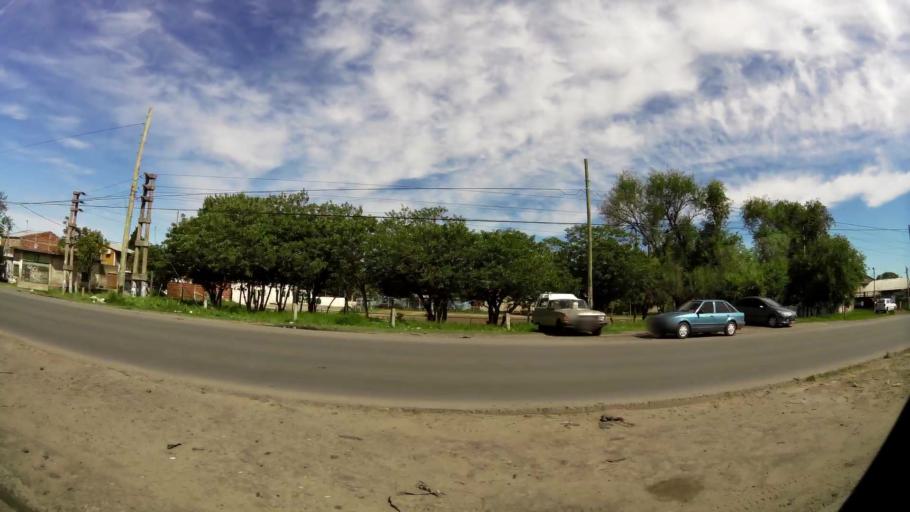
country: AR
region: Buenos Aires
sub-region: Partido de Quilmes
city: Quilmes
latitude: -34.7828
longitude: -58.2974
